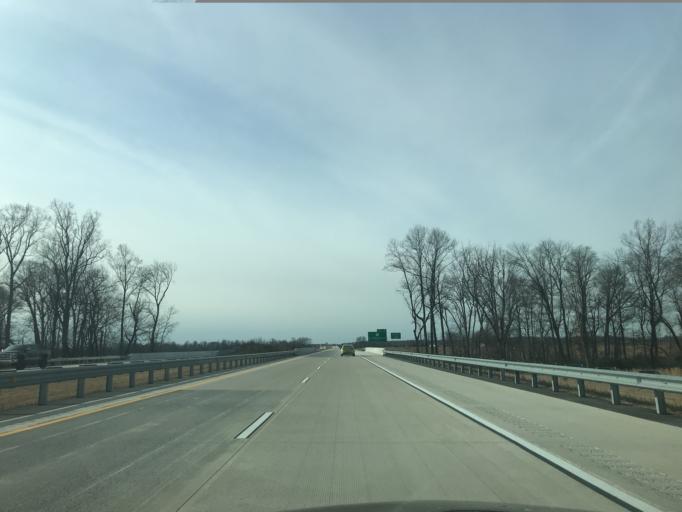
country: US
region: Delaware
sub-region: New Castle County
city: Middletown
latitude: 39.4972
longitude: -75.7009
